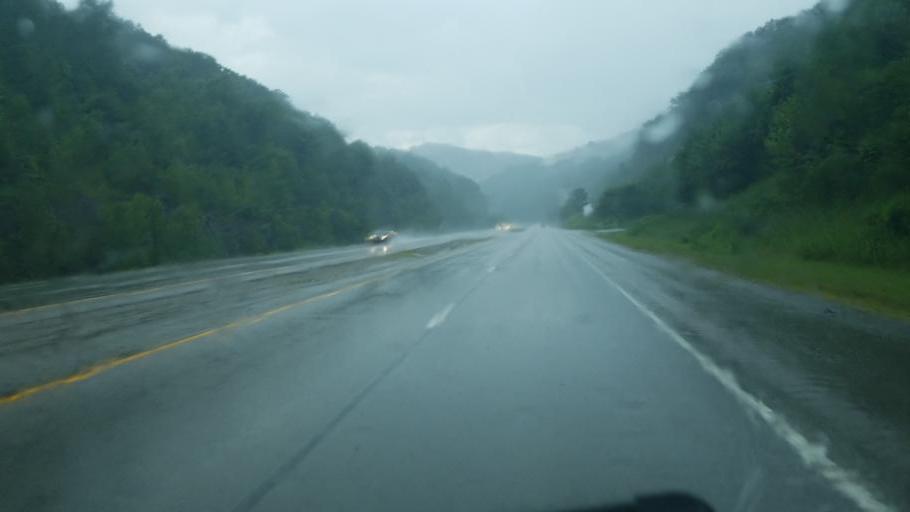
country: US
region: West Virginia
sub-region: Mingo County
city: Williamson
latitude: 37.6086
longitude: -82.3645
